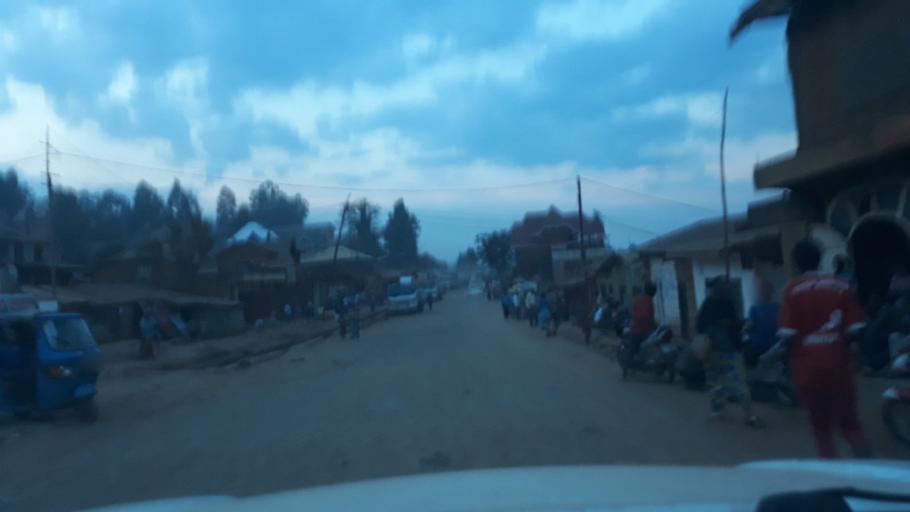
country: CD
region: South Kivu
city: Bukavu
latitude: -2.5436
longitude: 28.8639
